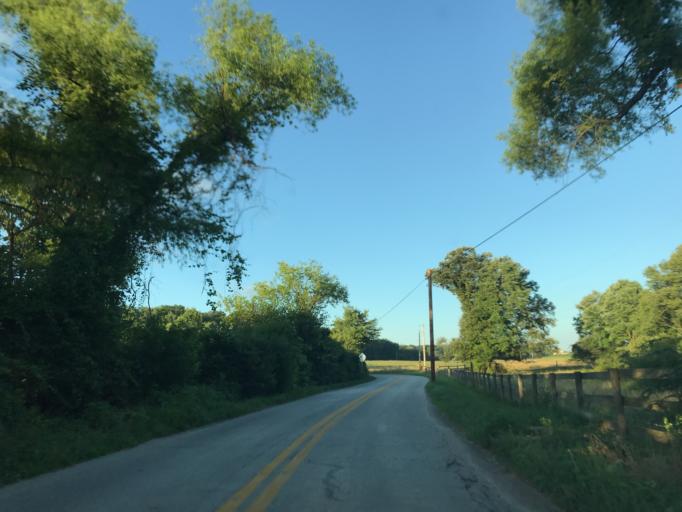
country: US
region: Maryland
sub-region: Baltimore County
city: Hunt Valley
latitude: 39.5641
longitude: -76.6915
